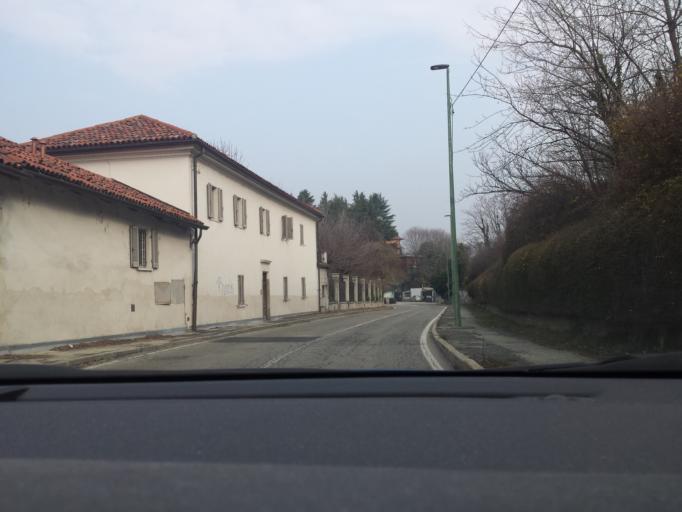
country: IT
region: Piedmont
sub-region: Provincia di Torino
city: Turin
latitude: 45.0533
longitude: 7.7164
